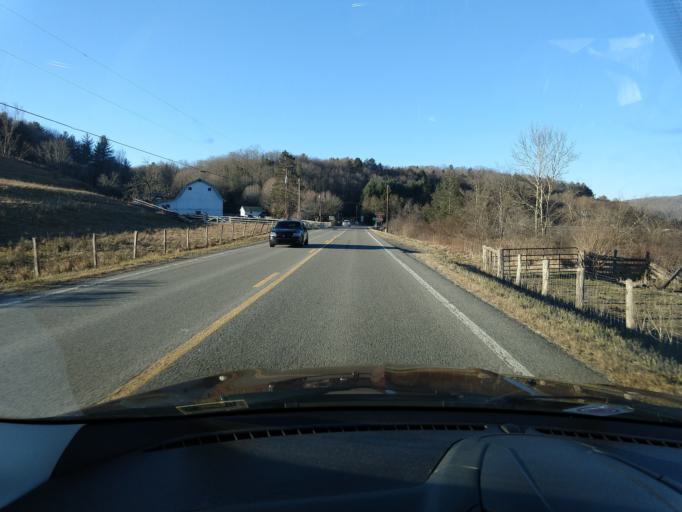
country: US
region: Virginia
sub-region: Highland County
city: Monterey
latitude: 38.5404
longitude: -79.7763
